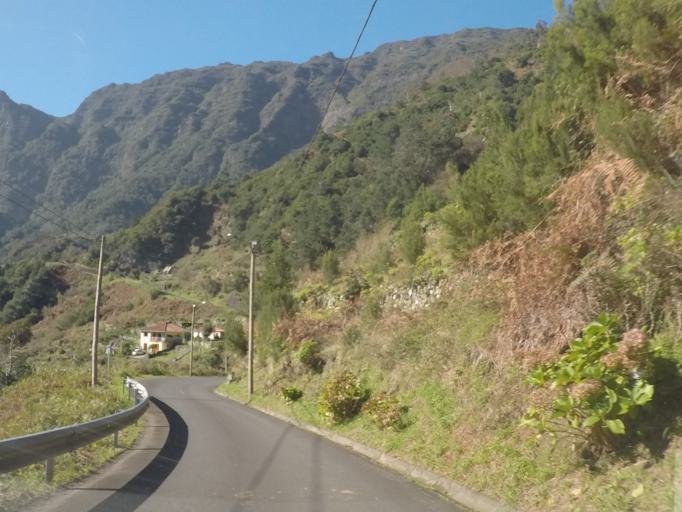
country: PT
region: Madeira
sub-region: Camara de Lobos
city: Curral das Freiras
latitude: 32.7848
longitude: -16.9763
